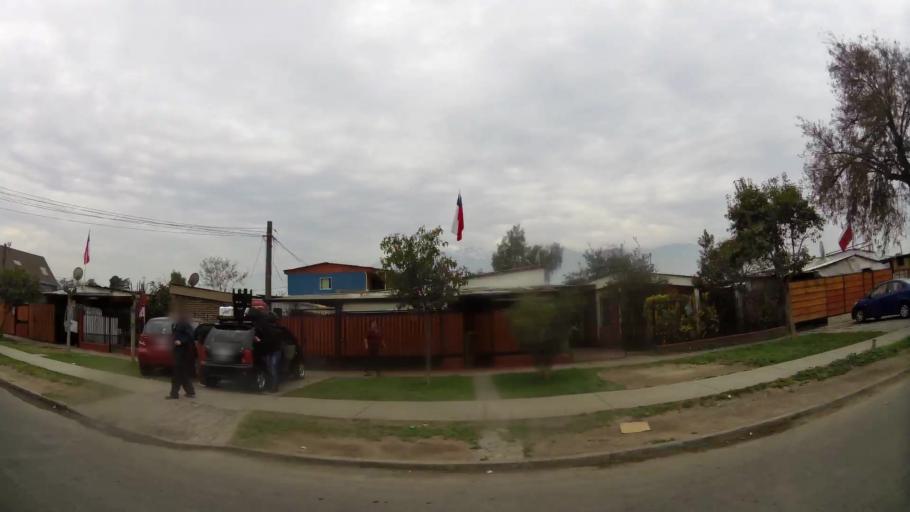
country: CL
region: Santiago Metropolitan
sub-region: Provincia de Santiago
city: Villa Presidente Frei, Nunoa, Santiago, Chile
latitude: -33.4748
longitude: -70.5922
